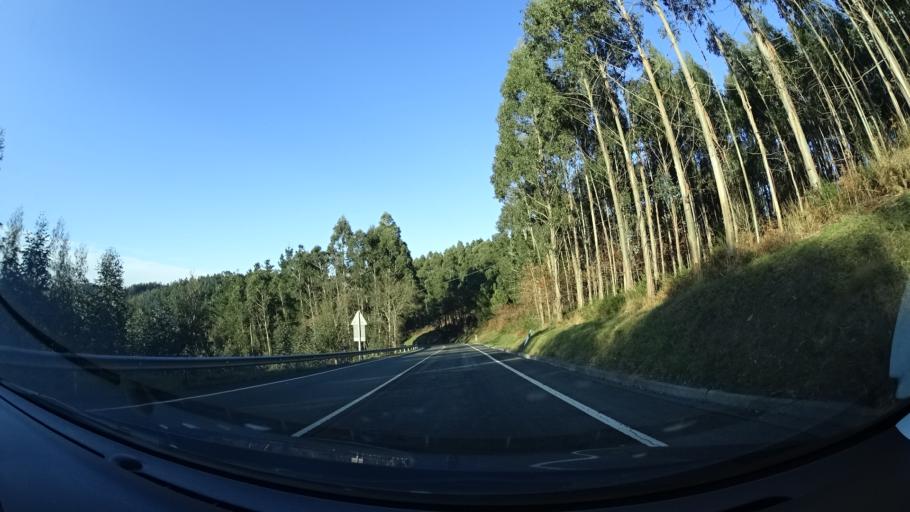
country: ES
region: Basque Country
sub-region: Bizkaia
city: Bakio
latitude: 43.3855
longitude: -2.7781
